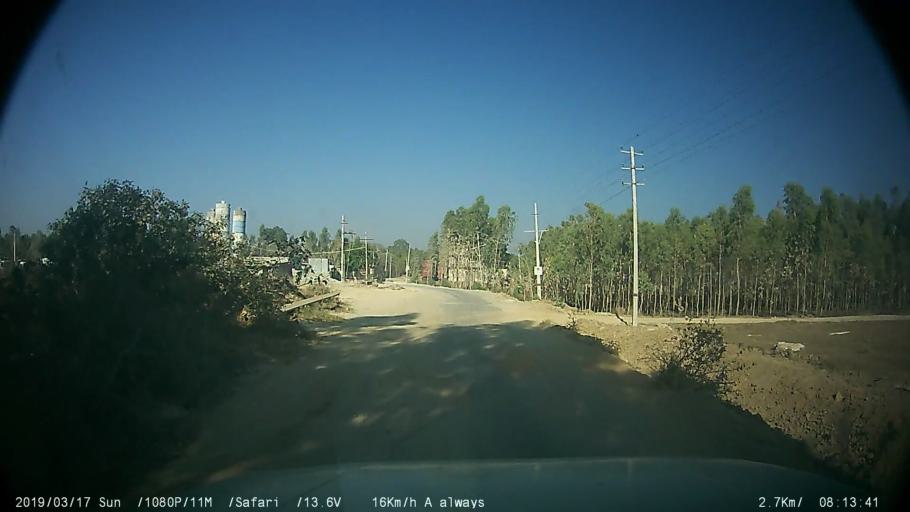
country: IN
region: Karnataka
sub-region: Bangalore Urban
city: Anekal
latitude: 12.8142
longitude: 77.6318
